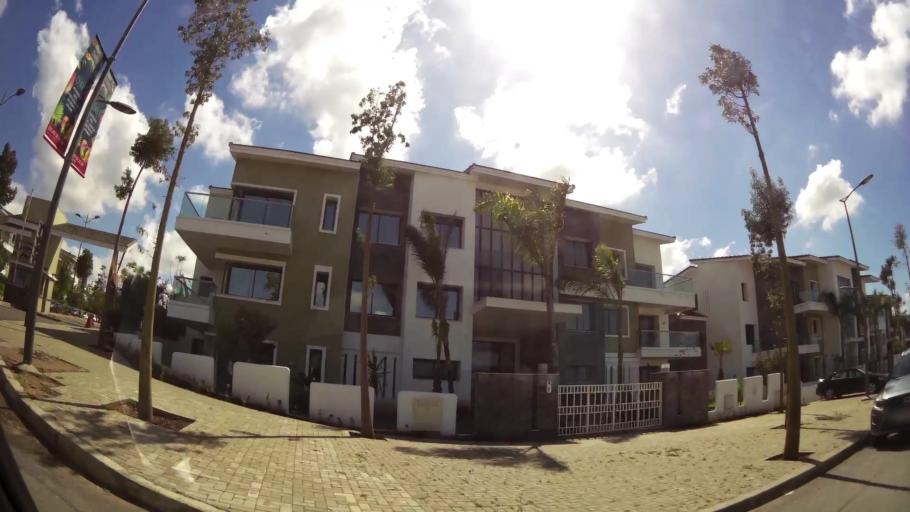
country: MA
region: Grand Casablanca
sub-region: Nouaceur
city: Bouskoura
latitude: 33.4832
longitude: -7.5924
